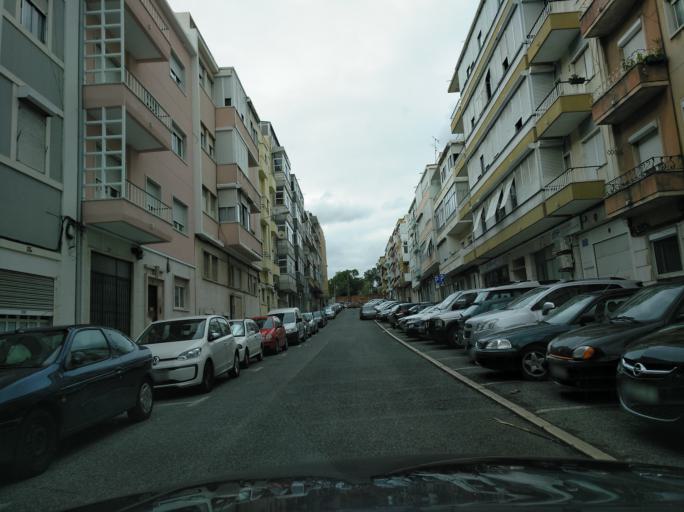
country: PT
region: Lisbon
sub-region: Odivelas
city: Olival do Basto
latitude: 38.7603
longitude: -9.1392
